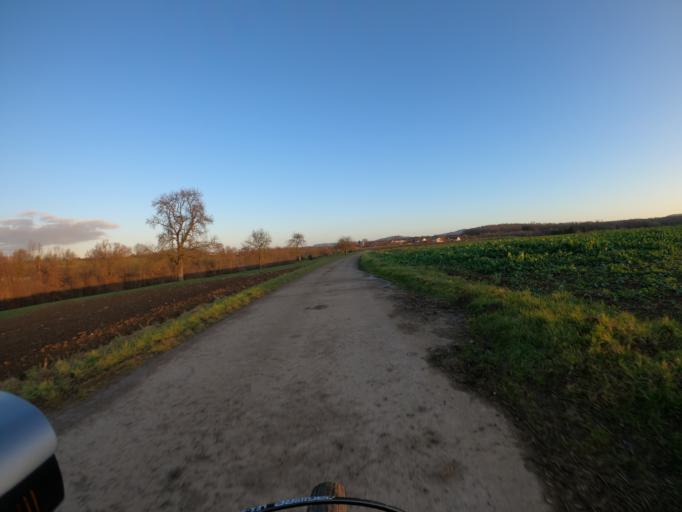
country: DE
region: Baden-Wuerttemberg
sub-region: Regierungsbezirk Stuttgart
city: Schlierbach
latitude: 48.6746
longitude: 9.5040
